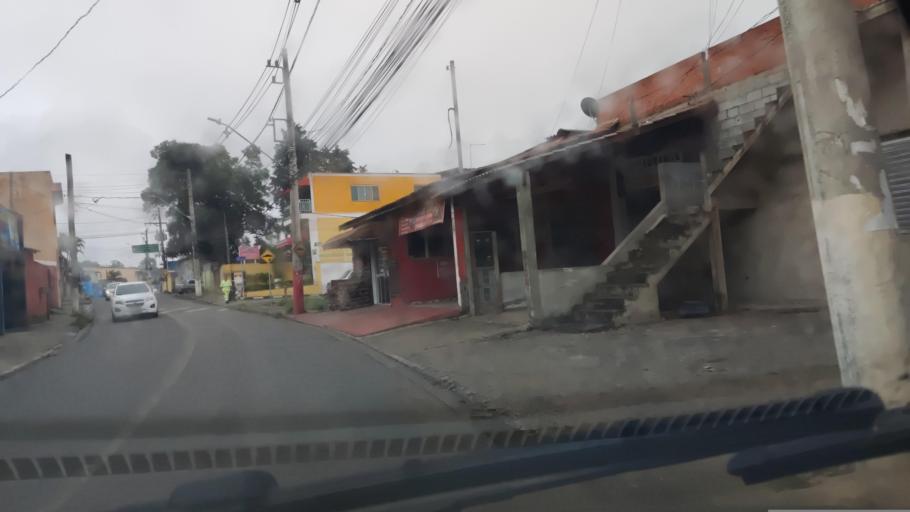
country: BR
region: Sao Paulo
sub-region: Vargem Grande Paulista
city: Vargem Grande Paulista
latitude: -23.6823
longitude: -47.0258
